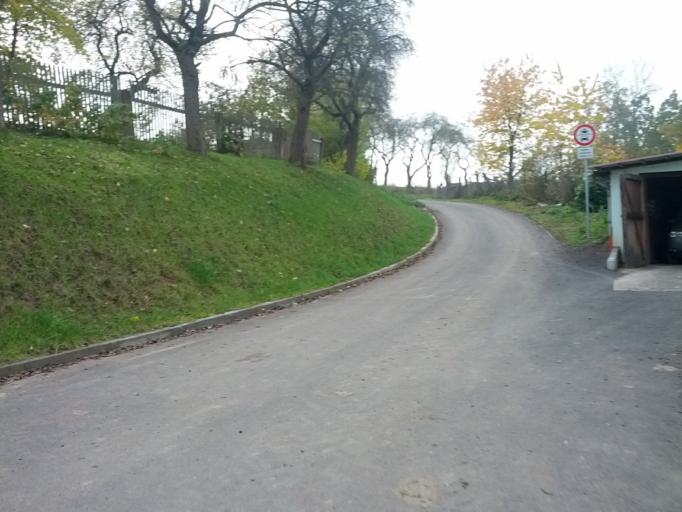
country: DE
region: Thuringia
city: Bischofroda
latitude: 51.0096
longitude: 10.4011
